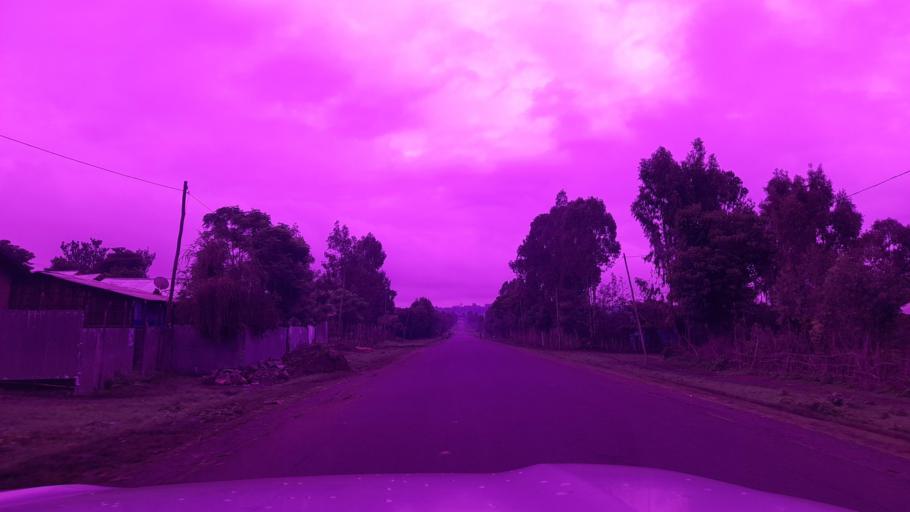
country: ET
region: Oromiya
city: Waliso
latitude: 8.2806
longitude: 37.6900
